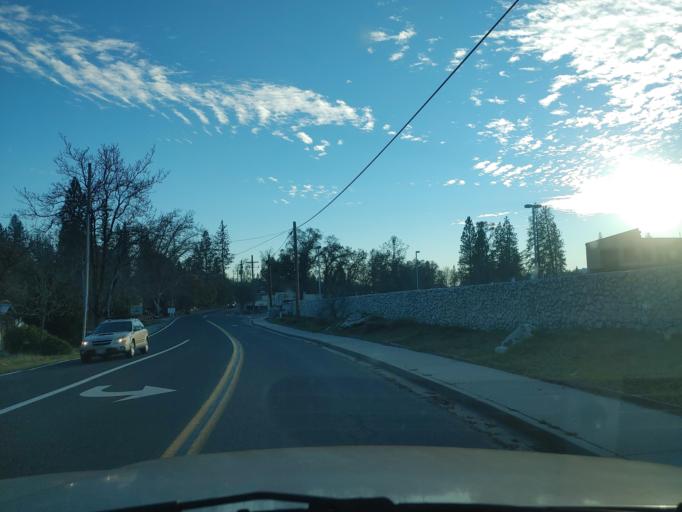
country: US
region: California
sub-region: Tuolumne County
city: Columbia
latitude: 38.0315
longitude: -120.4060
